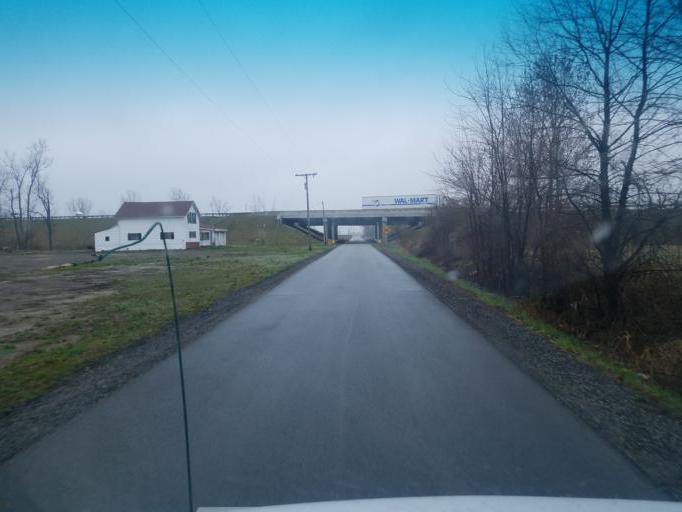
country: US
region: Ohio
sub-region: Wood County
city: North Baltimore
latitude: 41.2685
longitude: -83.6490
